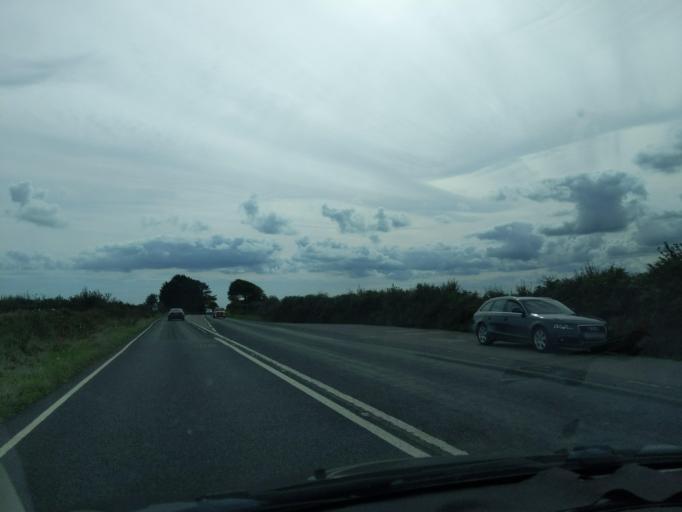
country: GB
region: England
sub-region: Cornwall
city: Par
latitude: 50.3820
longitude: -4.7005
